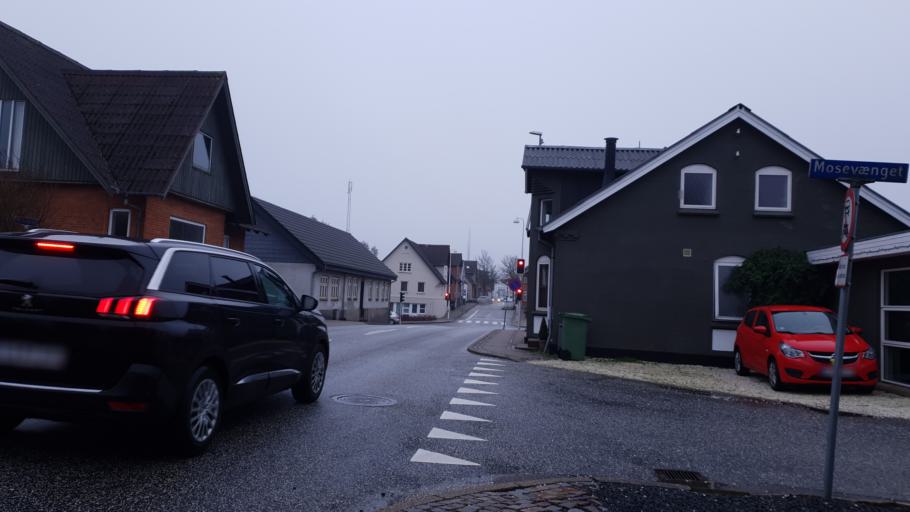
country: DK
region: Central Jutland
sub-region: Hedensted Kommune
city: Hedensted
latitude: 55.7714
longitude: 9.6982
